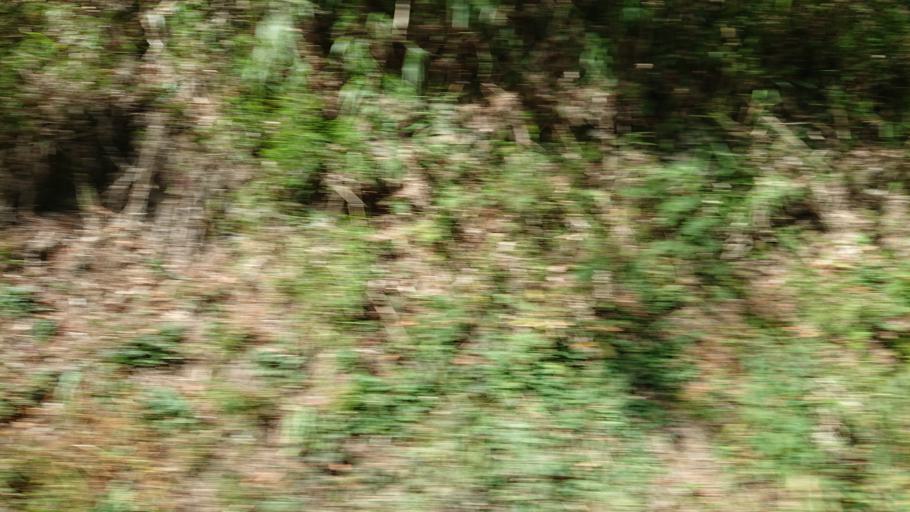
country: TW
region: Taiwan
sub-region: Hualien
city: Hualian
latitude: 24.3476
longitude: 121.3100
